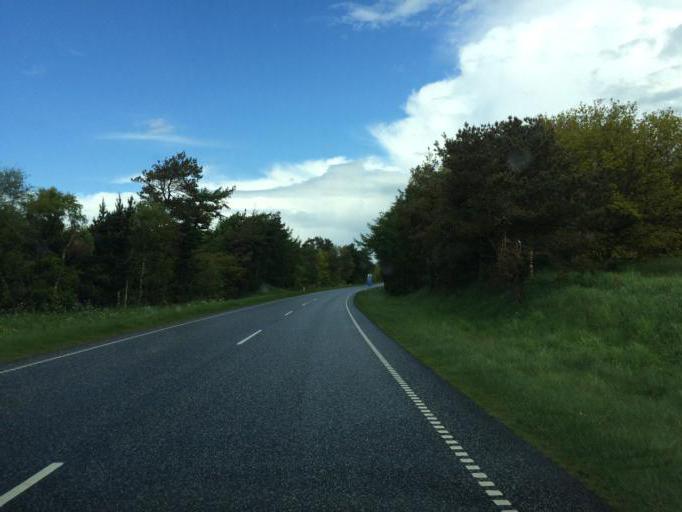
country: DK
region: North Denmark
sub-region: Vesthimmerland Kommune
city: Farso
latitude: 56.6367
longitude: 9.3557
